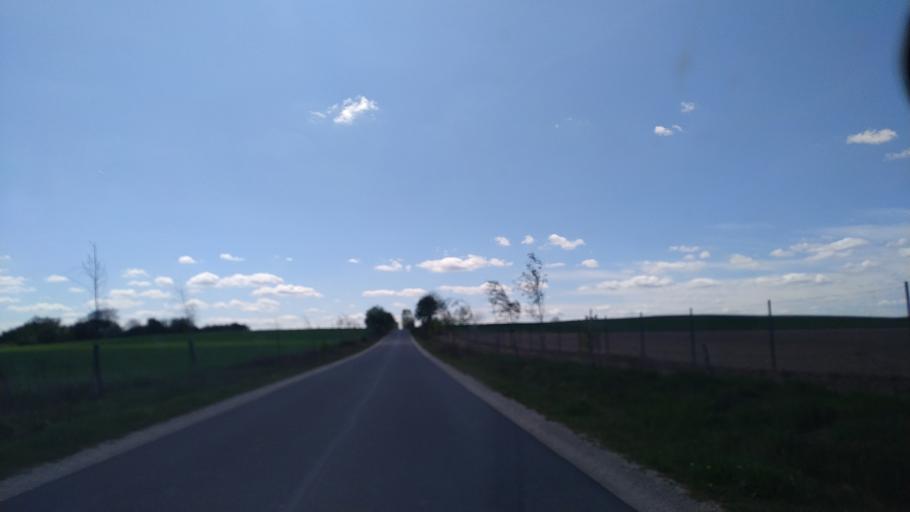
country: PL
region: Greater Poland Voivodeship
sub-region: Powiat pilski
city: Pila
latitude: 53.2397
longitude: 16.6972
